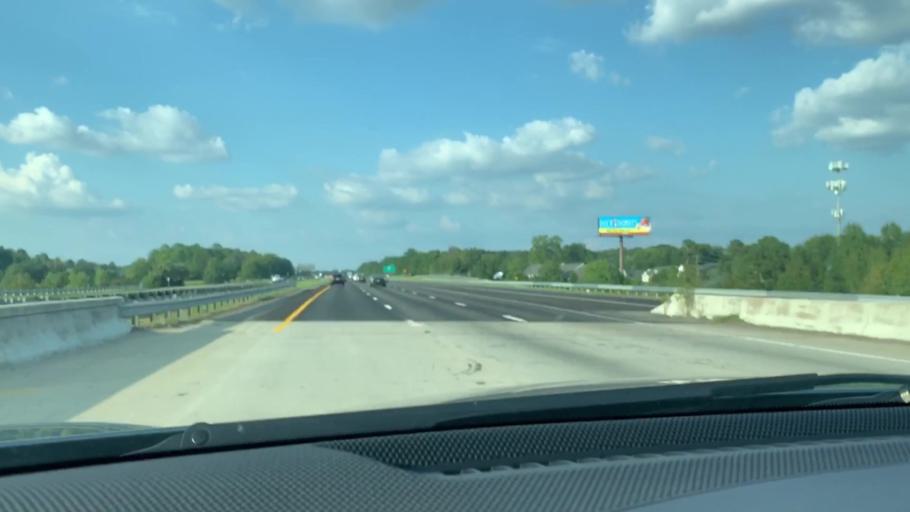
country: US
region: South Carolina
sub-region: Richland County
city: Forest Acres
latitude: 33.9761
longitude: -80.9549
